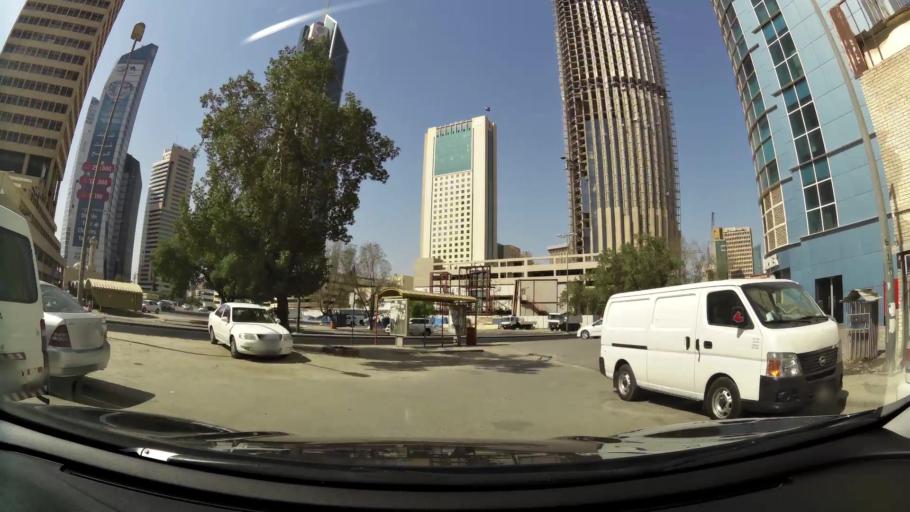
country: KW
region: Al Asimah
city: Ad Dasmah
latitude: 29.3766
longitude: 47.9938
